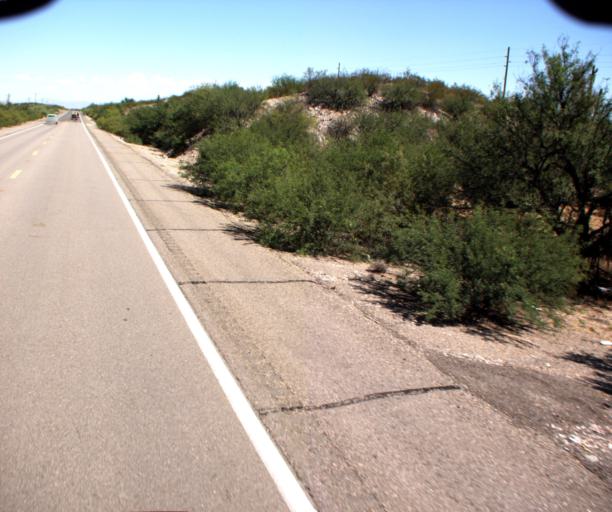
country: US
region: Arizona
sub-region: Pinal County
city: Mammoth
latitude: 32.8014
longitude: -110.6796
